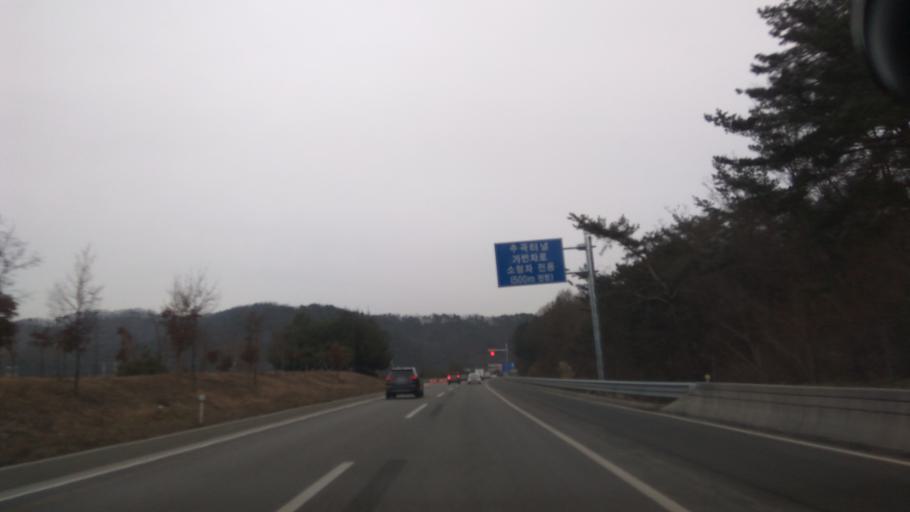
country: KR
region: Gangwon-do
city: Sindong
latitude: 37.7402
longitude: 127.6507
